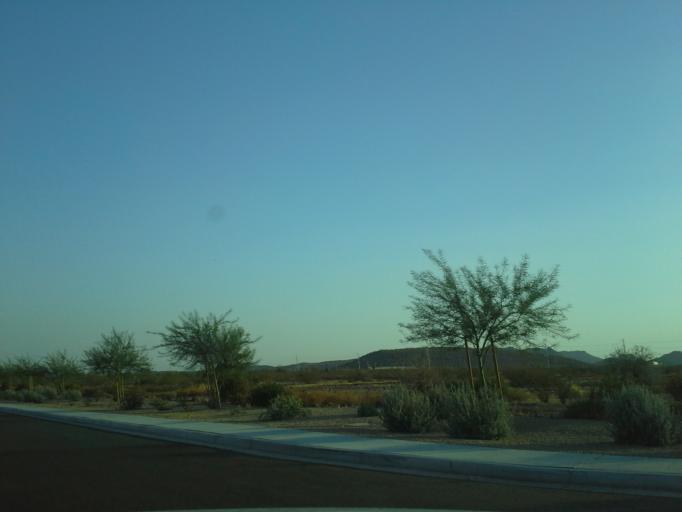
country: US
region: Arizona
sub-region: Maricopa County
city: Anthem
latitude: 33.7644
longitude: -112.1171
